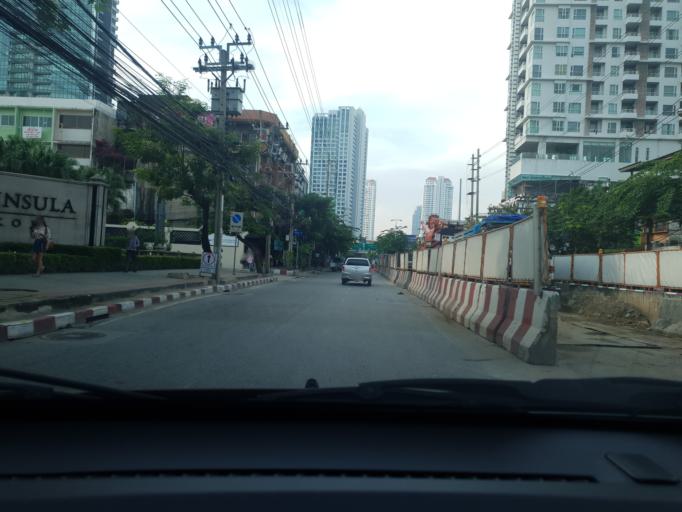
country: TH
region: Bangkok
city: Khlong San
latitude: 13.7233
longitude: 100.5091
